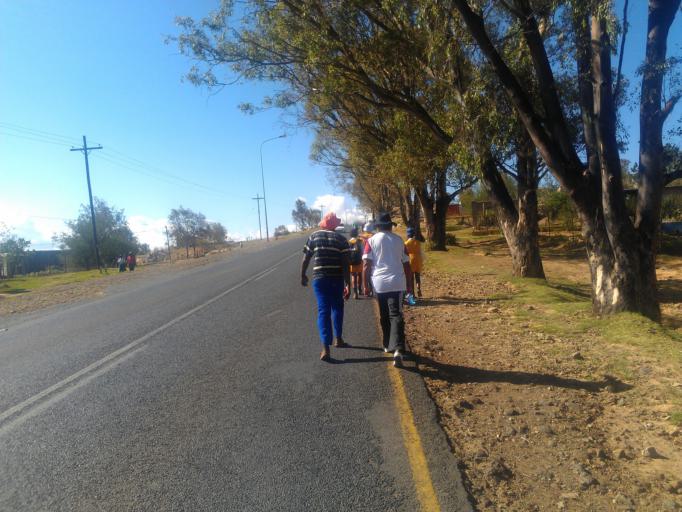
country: LS
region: Berea
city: Teyateyaneng
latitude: -29.1342
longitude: 27.7585
